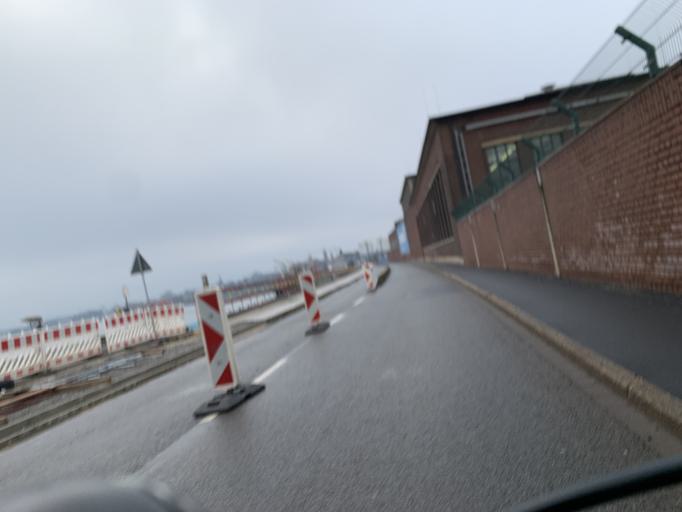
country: DE
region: North Rhine-Westphalia
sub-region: Regierungsbezirk Dusseldorf
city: Krefeld
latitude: 51.3649
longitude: 6.6566
